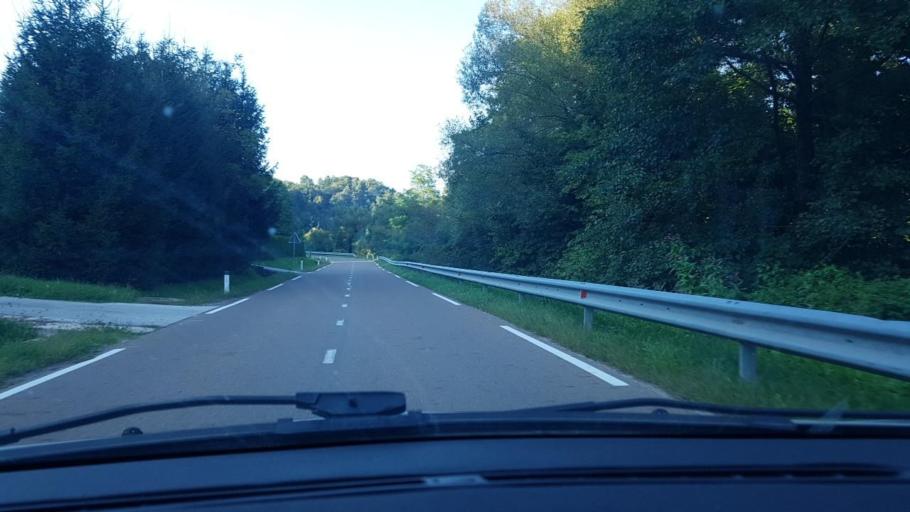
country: SI
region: Podlehnik
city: Podlehnik
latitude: 46.3140
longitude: 15.9400
